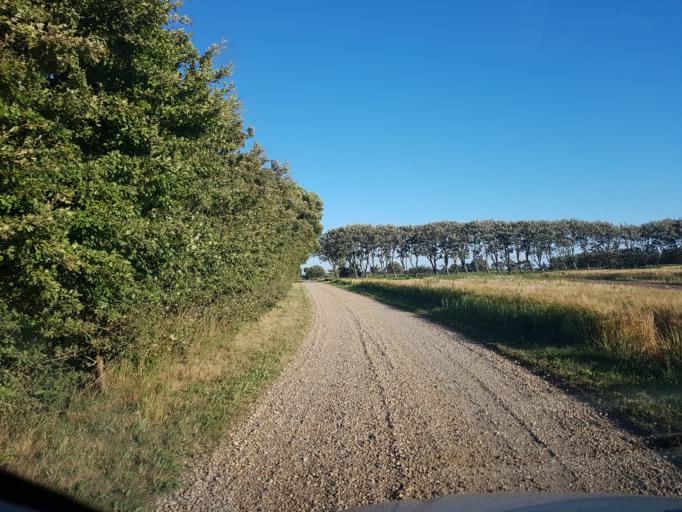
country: DK
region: South Denmark
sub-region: Esbjerg Kommune
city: Esbjerg
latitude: 55.4924
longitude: 8.5043
